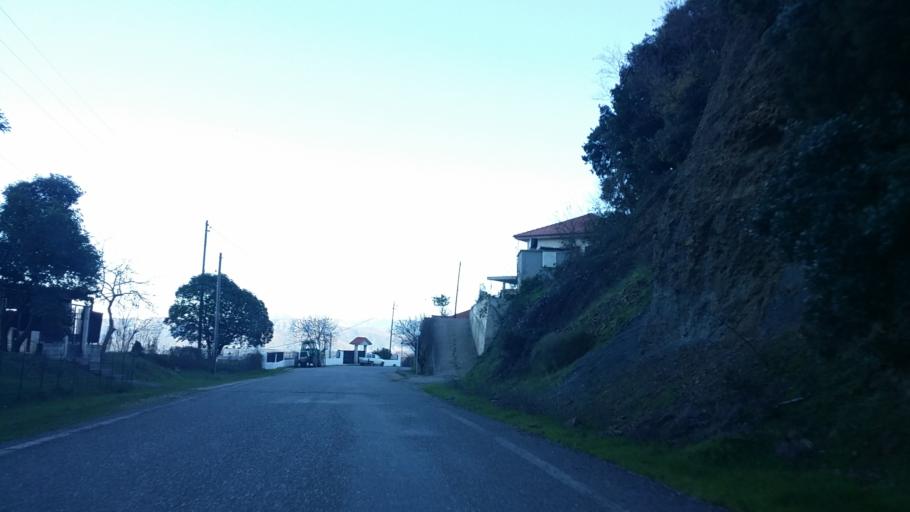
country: GR
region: West Greece
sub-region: Nomos Aitolias kai Akarnanias
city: Sardinia
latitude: 38.8696
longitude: 21.2846
